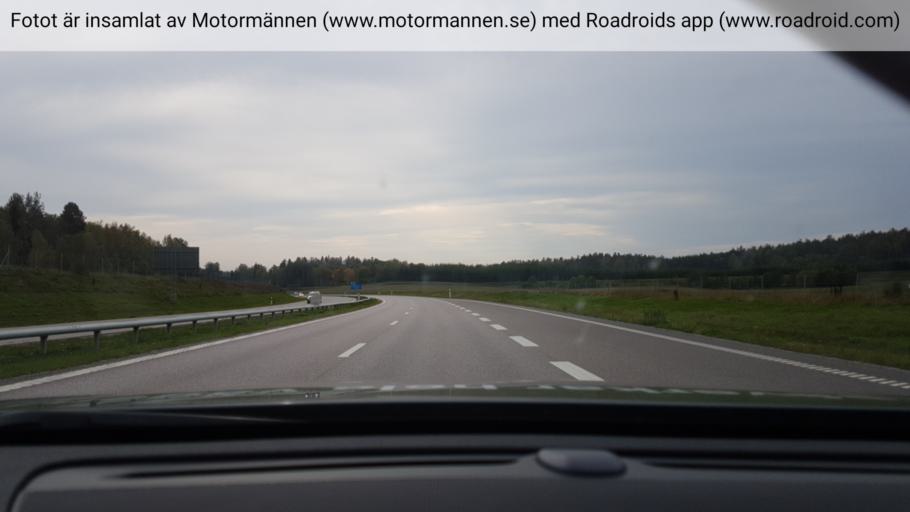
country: SE
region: Stockholm
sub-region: Nynashamns Kommun
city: Osmo
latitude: 58.9556
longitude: 17.9026
